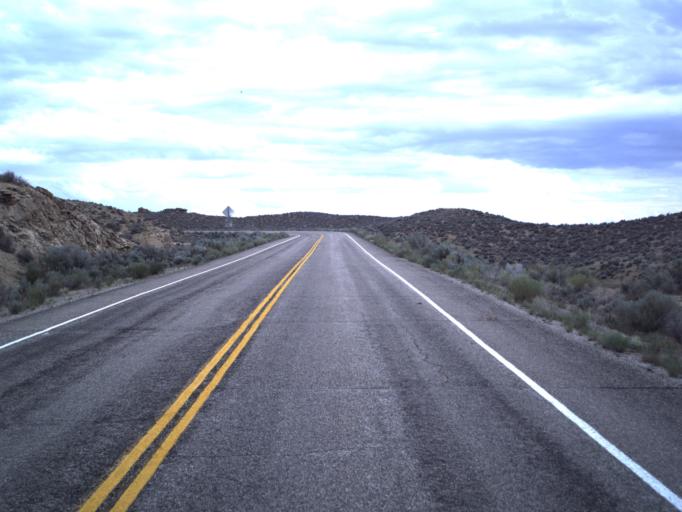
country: US
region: Colorado
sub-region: Rio Blanco County
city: Rangely
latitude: 39.9729
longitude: -109.1715
